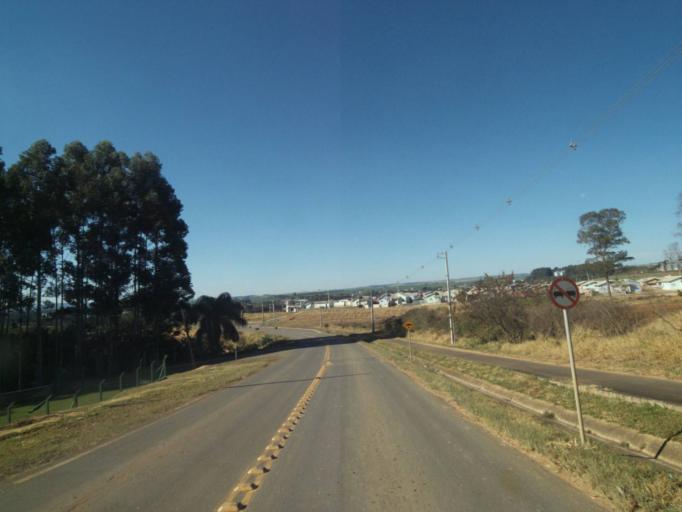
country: BR
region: Parana
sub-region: Tibagi
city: Tibagi
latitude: -24.5211
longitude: -50.4273
